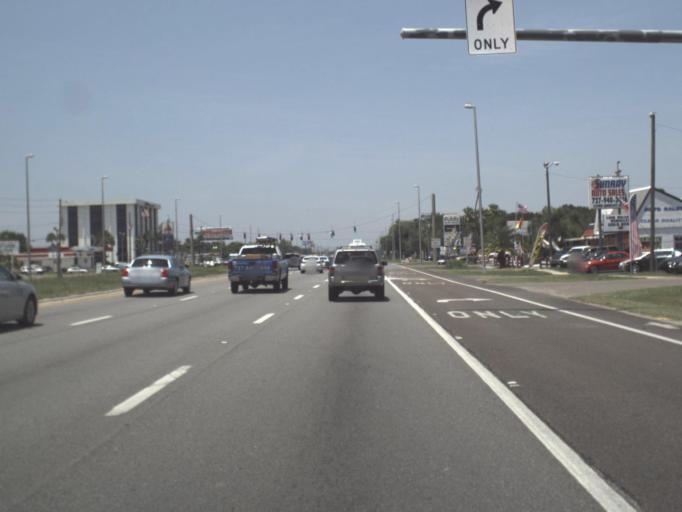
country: US
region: Florida
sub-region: Pasco County
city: Holiday
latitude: 28.1962
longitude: -82.7397
